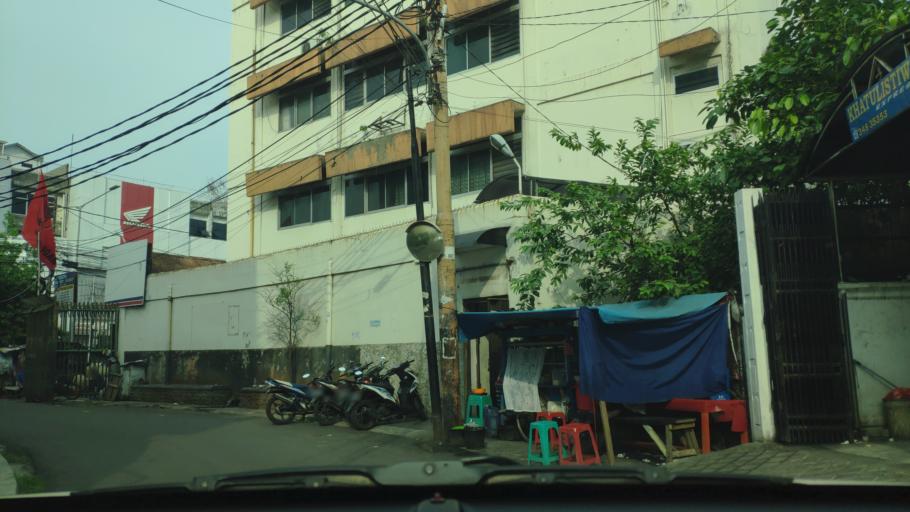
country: ID
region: Jakarta Raya
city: Jakarta
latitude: -6.1605
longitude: 106.8219
